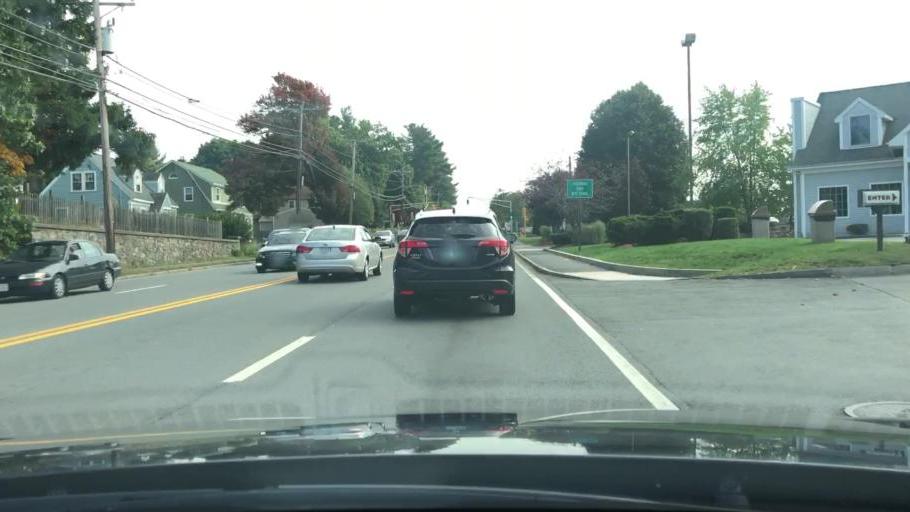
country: US
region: Massachusetts
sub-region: Essex County
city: Methuen
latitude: 42.7377
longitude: -71.1951
